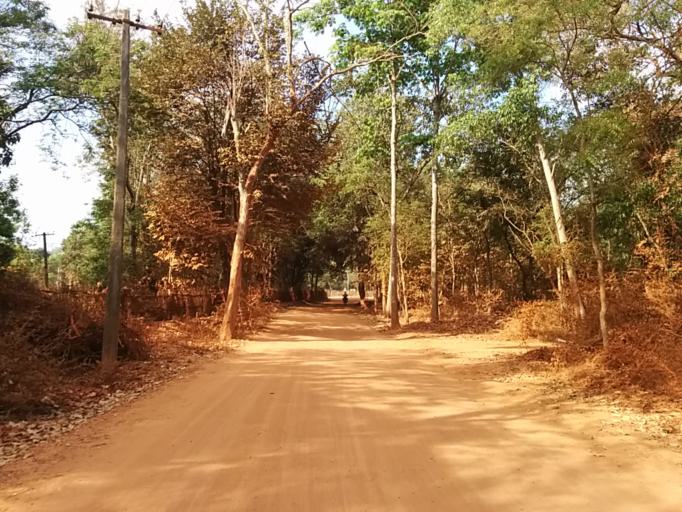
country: IN
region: Tamil Nadu
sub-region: Villupuram
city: Auroville
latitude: 12.0060
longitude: 79.8079
